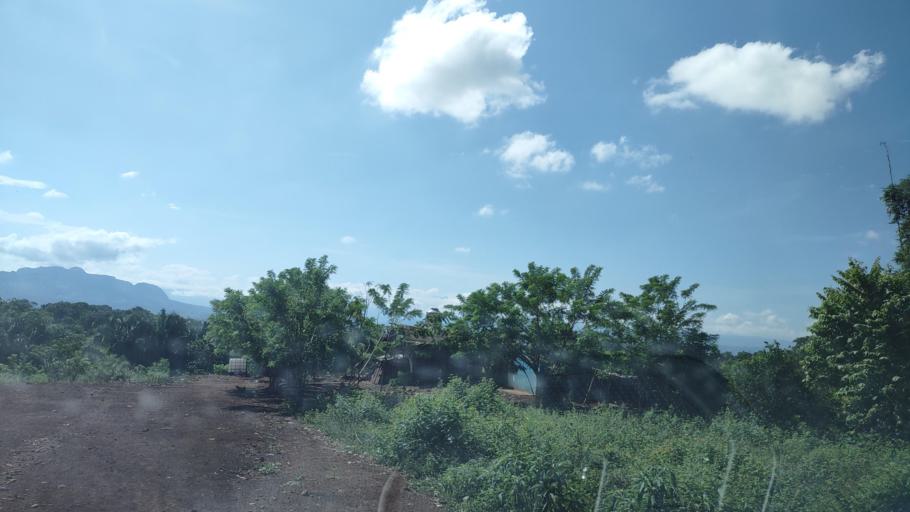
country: MX
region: Veracruz
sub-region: Martinez de la Torre
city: La Union Paso Largo
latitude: 20.1274
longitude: -96.9909
